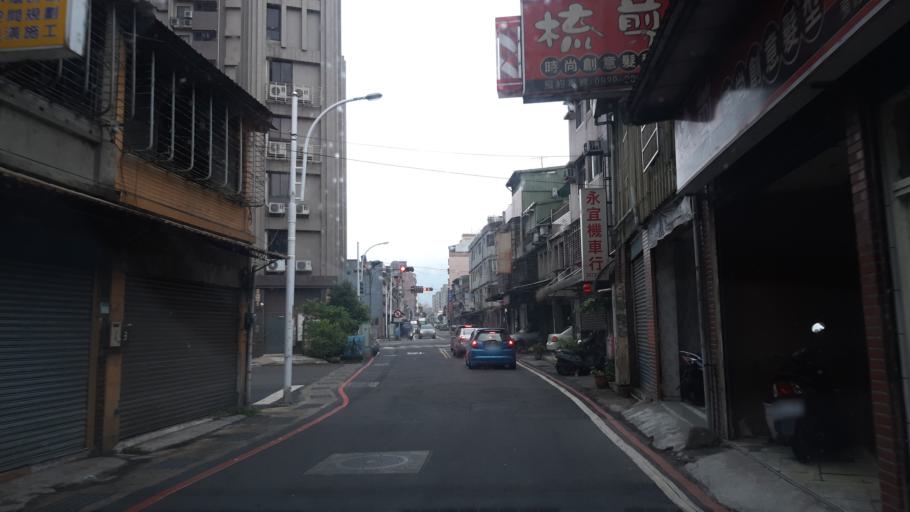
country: TW
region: Taiwan
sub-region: Taoyuan
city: Taoyuan
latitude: 24.9277
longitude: 121.3686
